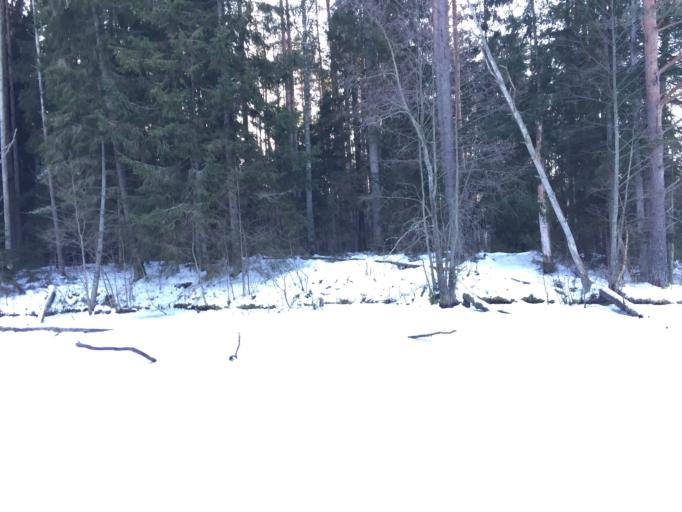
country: LV
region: Kegums
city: Kegums
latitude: 56.7287
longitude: 24.6407
